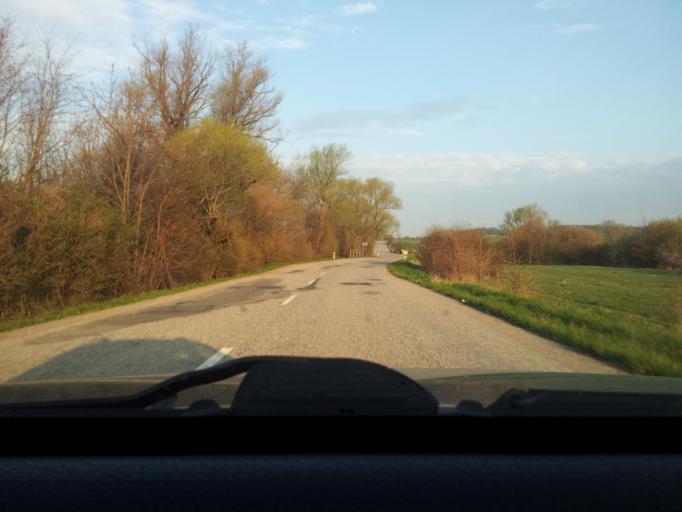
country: SK
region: Nitriansky
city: Tlmace
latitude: 48.2814
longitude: 18.4754
